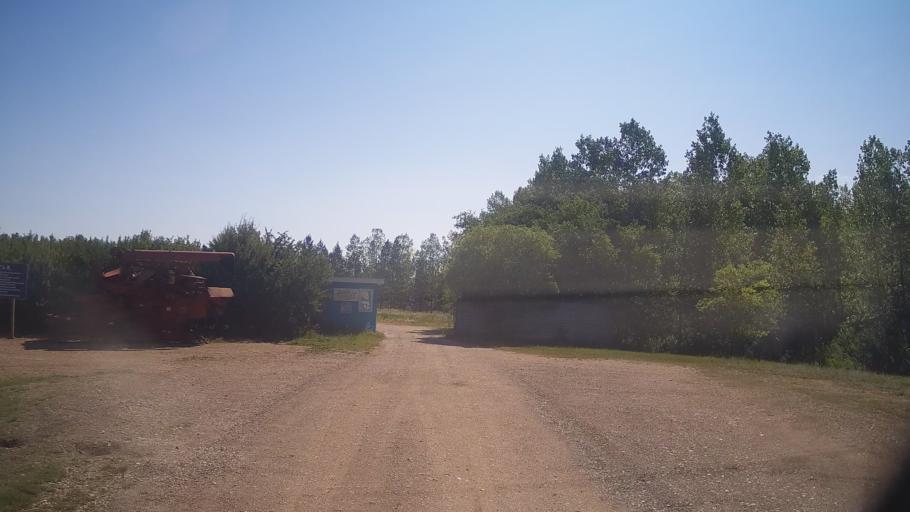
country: CA
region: Saskatchewan
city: Watrous
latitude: 51.7164
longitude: -105.4507
